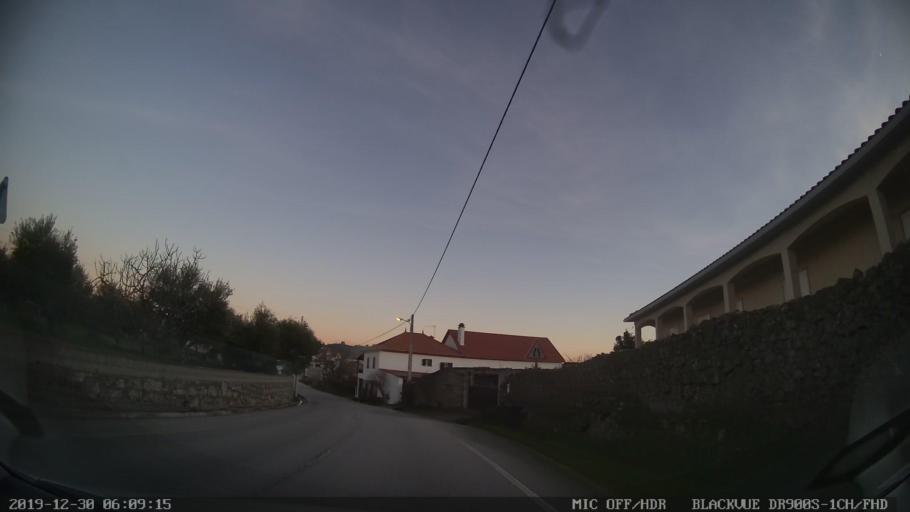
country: PT
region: Castelo Branco
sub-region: Penamacor
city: Penamacor
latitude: 40.1118
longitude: -7.2116
